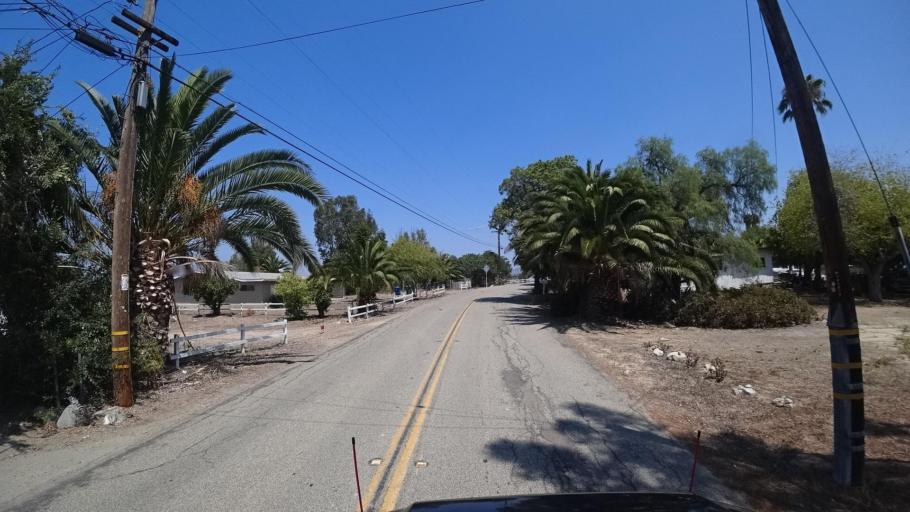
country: US
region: California
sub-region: San Diego County
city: Vista
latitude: 33.1813
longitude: -117.2623
